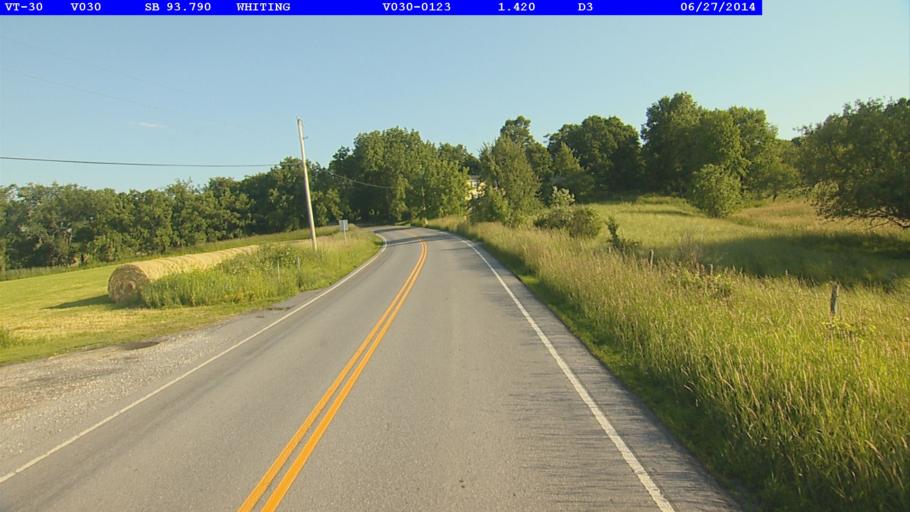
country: US
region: Vermont
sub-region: Rutland County
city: Brandon
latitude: 43.8579
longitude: -73.2022
